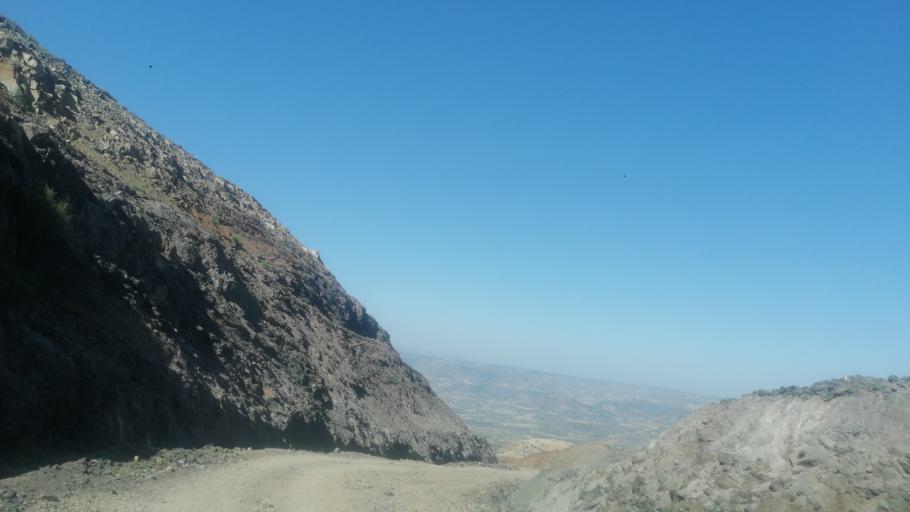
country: ET
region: Amhara
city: Addiet Canna
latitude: 11.1527
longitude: 37.8578
